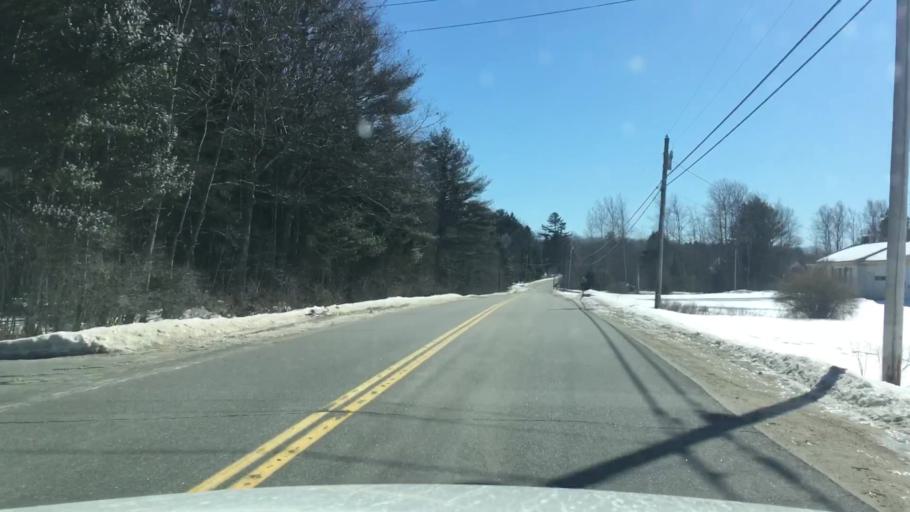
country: US
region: Maine
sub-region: Cumberland County
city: Brunswick
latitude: 43.8715
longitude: -70.0167
